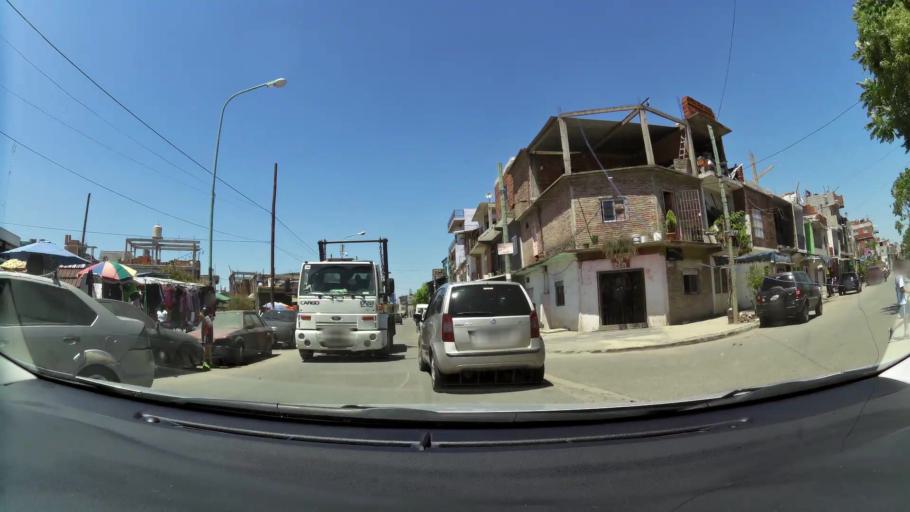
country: AR
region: Buenos Aires
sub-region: Partido de Avellaneda
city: Avellaneda
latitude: -34.6562
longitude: -58.4011
